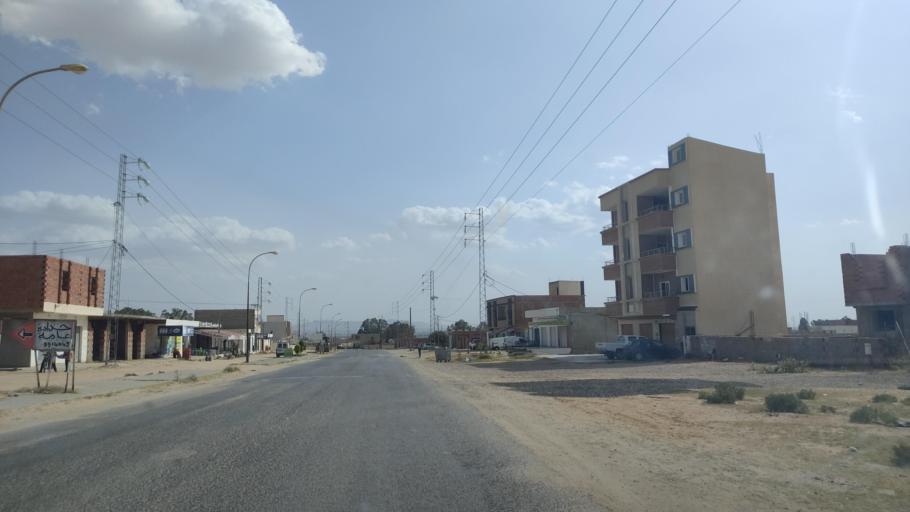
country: TN
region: Sidi Bu Zayd
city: Sidi Bouzid
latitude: 35.1037
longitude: 9.5359
